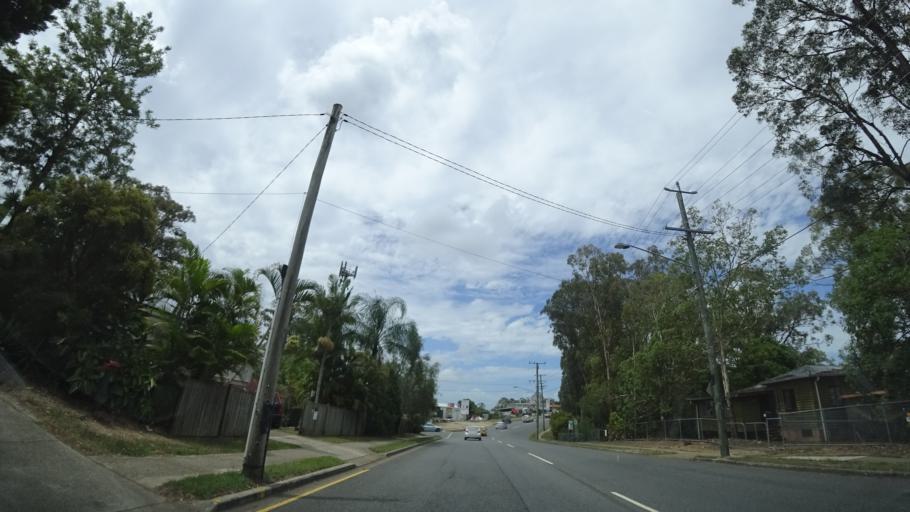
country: AU
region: Queensland
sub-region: Brisbane
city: Everton Park
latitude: -27.3907
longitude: 152.9765
